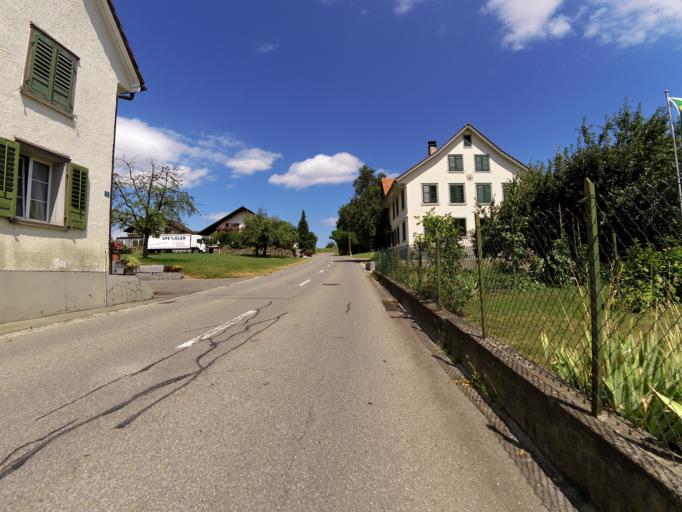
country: CH
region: Thurgau
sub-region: Weinfelden District
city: Maerstetten-Dorf
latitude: 47.6082
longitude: 9.0642
